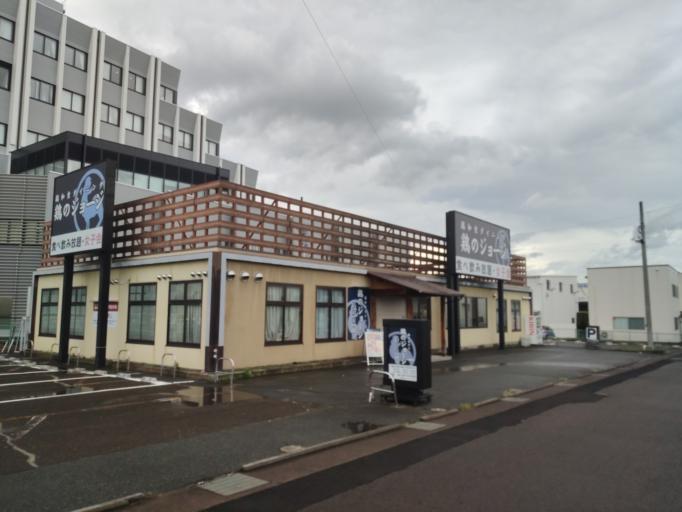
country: JP
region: Nagano
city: Saku
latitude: 36.2308
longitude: 138.4788
